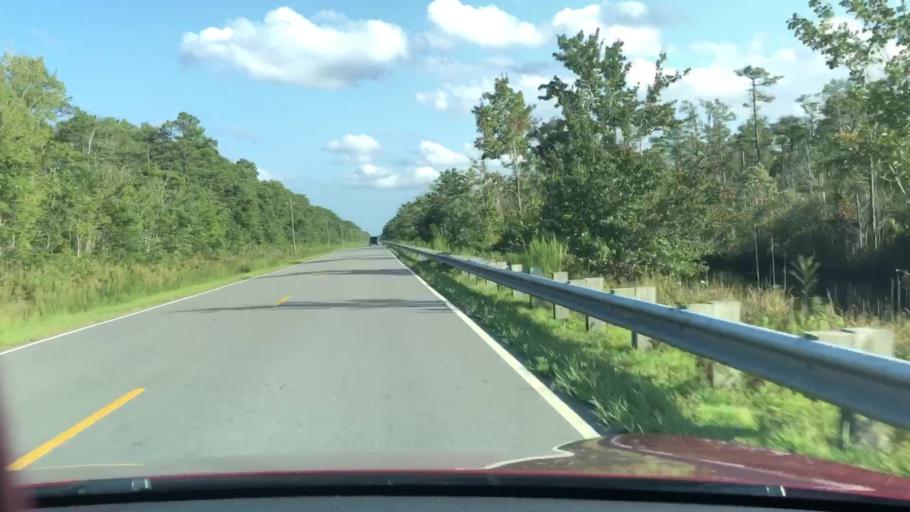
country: US
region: North Carolina
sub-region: Dare County
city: Manteo
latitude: 35.8074
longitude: -75.7881
